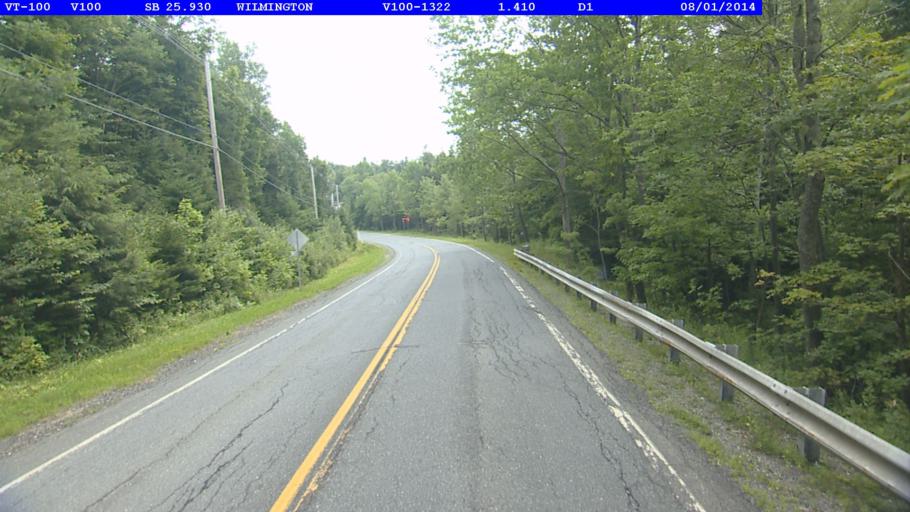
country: US
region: Vermont
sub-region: Windham County
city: Dover
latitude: 42.8471
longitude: -72.8592
